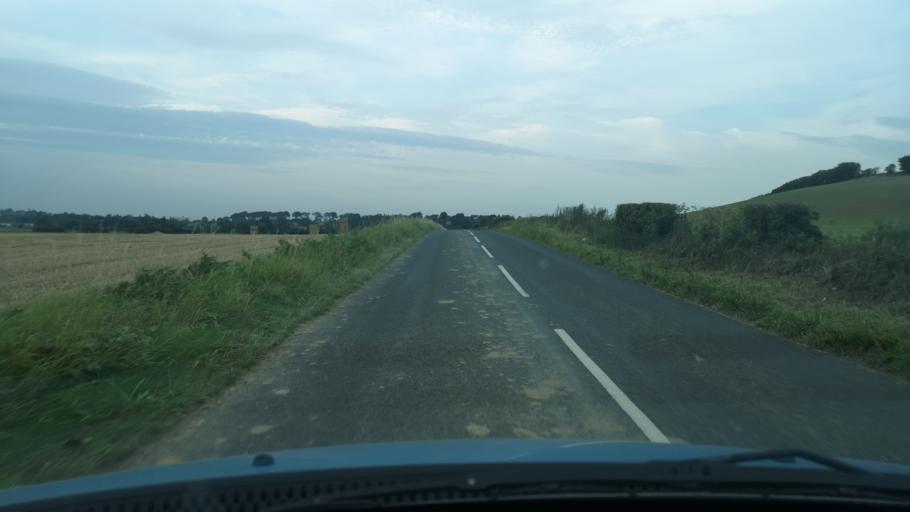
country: GB
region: England
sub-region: City and Borough of Wakefield
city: Darrington
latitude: 53.6665
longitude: -1.2874
